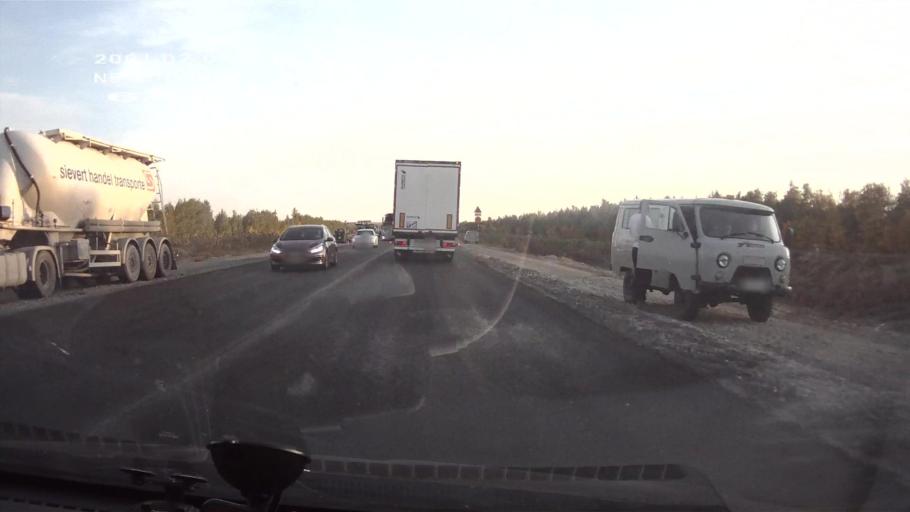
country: RU
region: Saratov
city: Krasnoarmeysk
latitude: 51.0104
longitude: 45.6177
